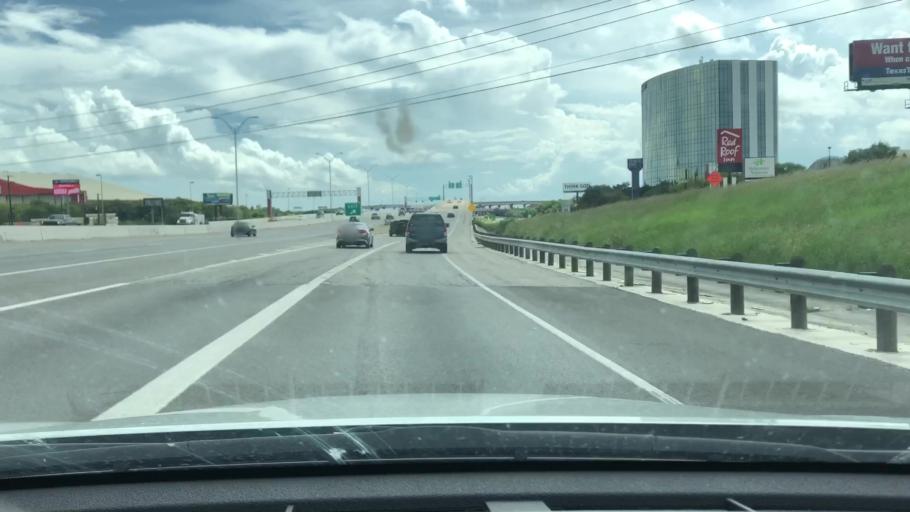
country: US
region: Texas
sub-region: Bexar County
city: Castle Hills
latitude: 29.5306
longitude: -98.4853
